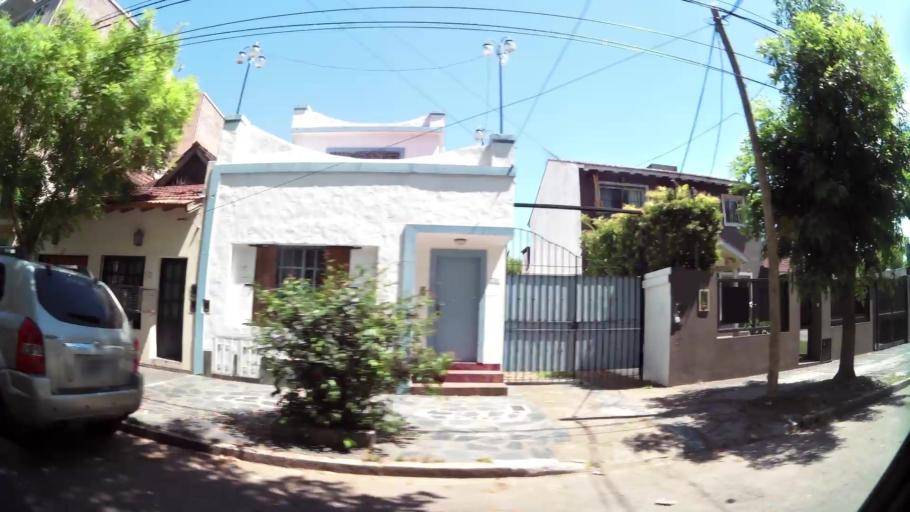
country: AR
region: Buenos Aires
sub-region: Partido de Tigre
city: Tigre
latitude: -34.4271
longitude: -58.5809
